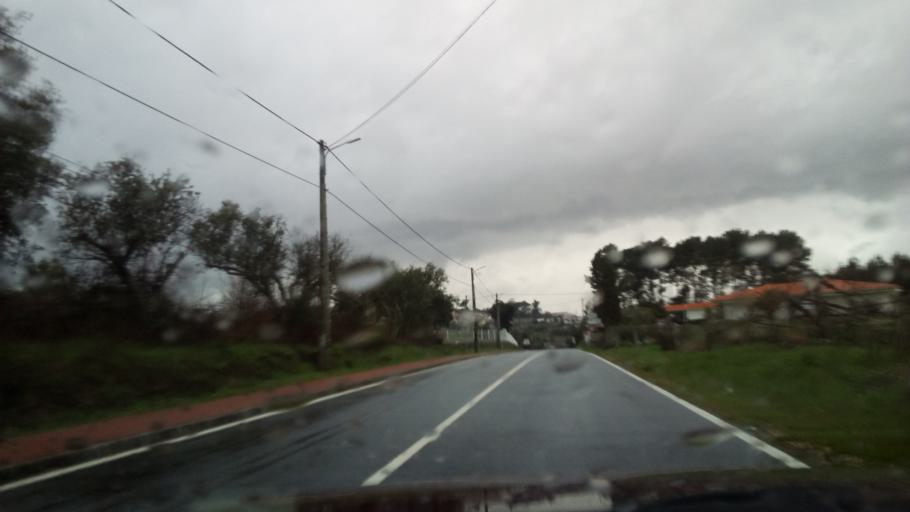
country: PT
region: Guarda
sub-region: Celorico da Beira
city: Celorico da Beira
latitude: 40.6404
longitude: -7.3744
